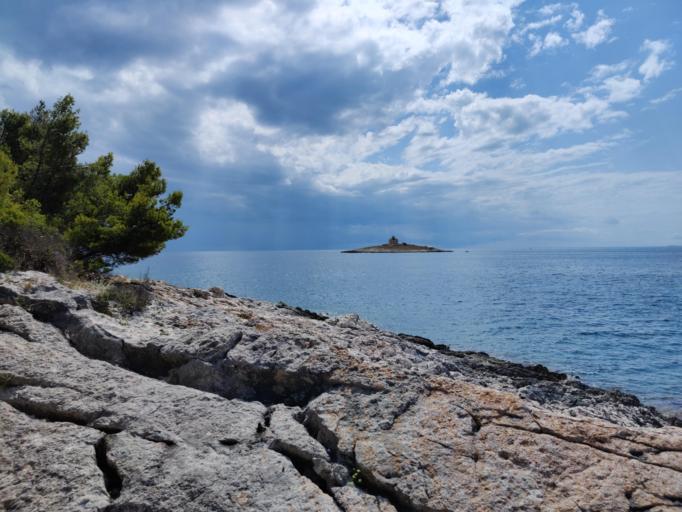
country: HR
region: Splitsko-Dalmatinska
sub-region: Grad Hvar
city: Hvar
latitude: 43.1625
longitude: 16.4559
